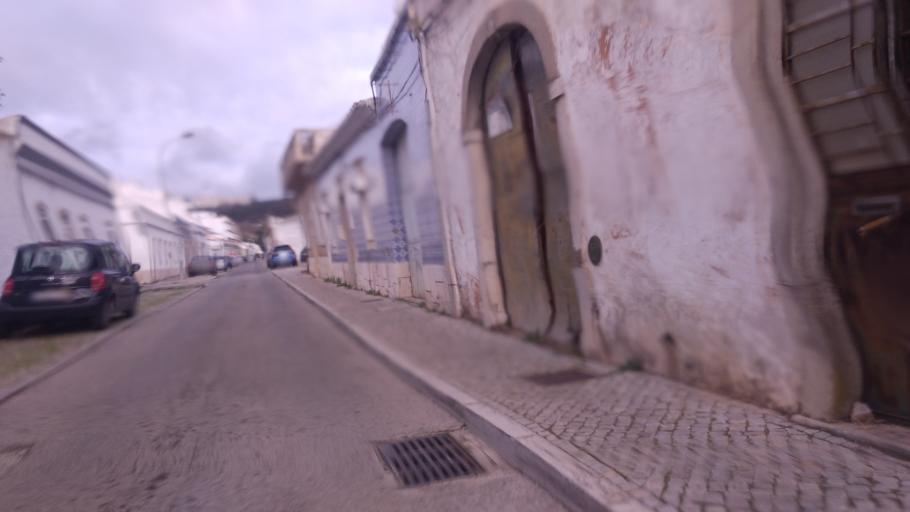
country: PT
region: Faro
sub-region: Sao Bras de Alportel
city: Sao Bras de Alportel
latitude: 37.1537
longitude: -7.8899
